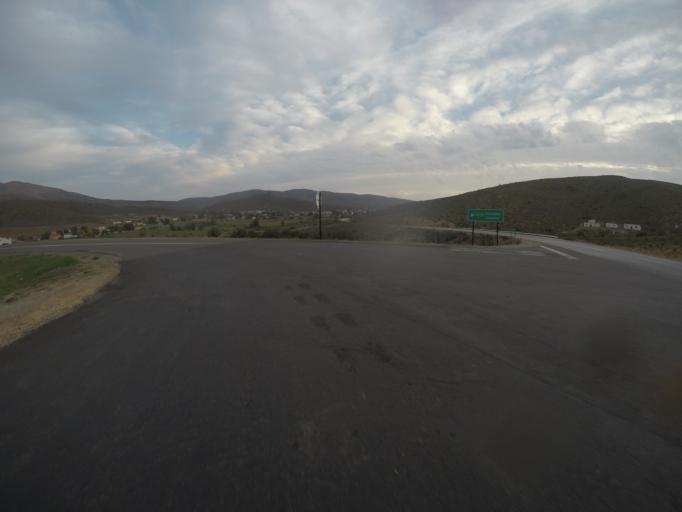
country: ZA
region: Western Cape
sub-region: Eden District Municipality
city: Knysna
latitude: -33.6419
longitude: 23.1344
